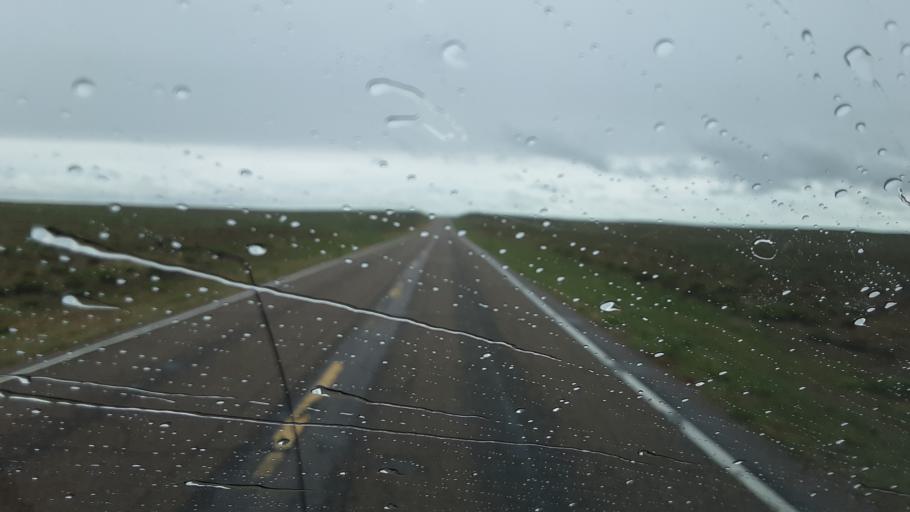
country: US
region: Colorado
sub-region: Lincoln County
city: Hugo
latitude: 38.8494
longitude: -103.2481
